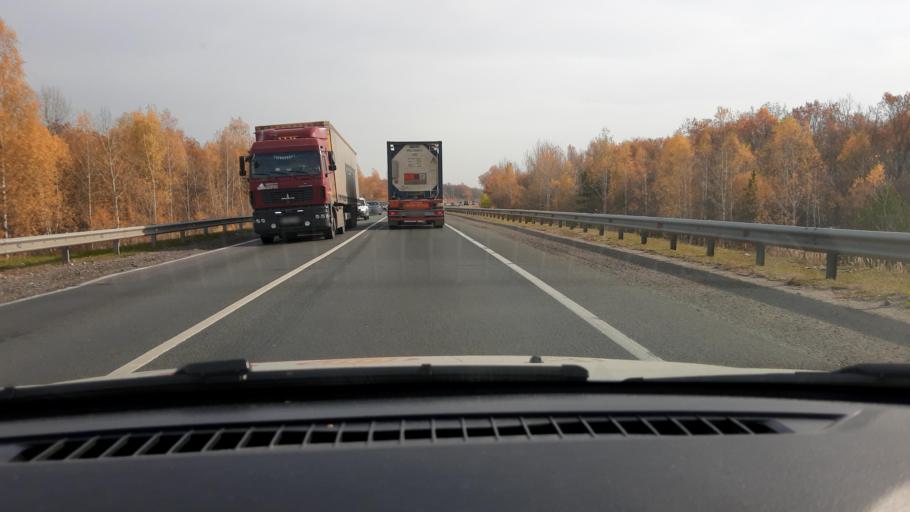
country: RU
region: Nizjnij Novgorod
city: Kstovo
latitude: 56.0950
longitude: 44.3160
